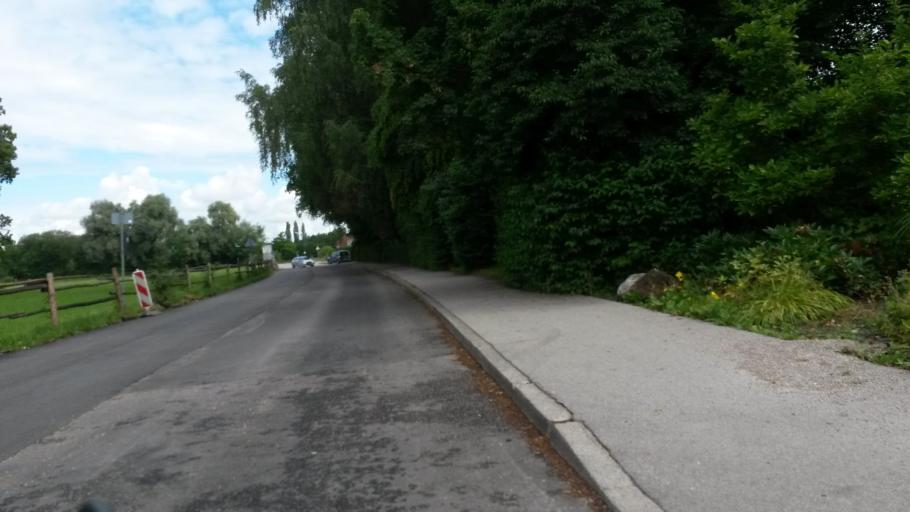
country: DE
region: Bavaria
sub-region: Upper Bavaria
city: Prien am Chiemsee
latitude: 47.8619
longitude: 12.3635
